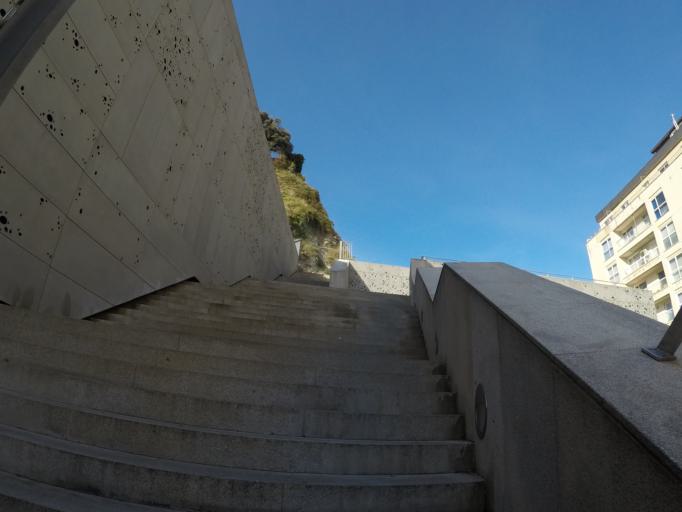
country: ES
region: Basque Country
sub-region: Provincia de Guipuzcoa
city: San Sebastian
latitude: 43.3253
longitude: -1.9846
